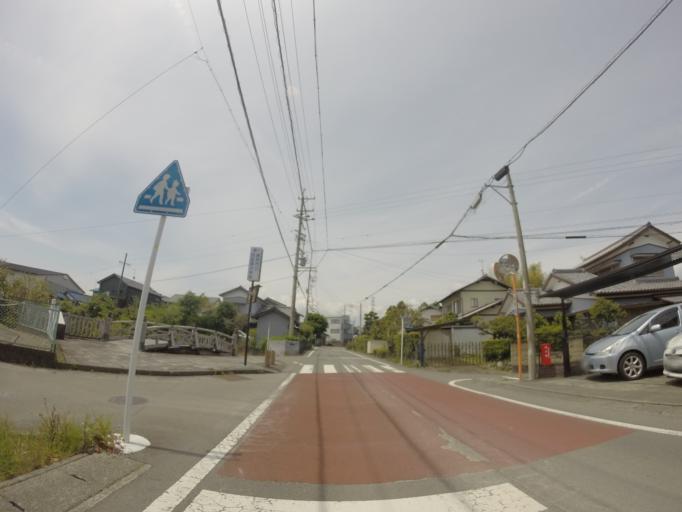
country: JP
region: Shizuoka
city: Fujieda
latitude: 34.8727
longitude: 138.2736
